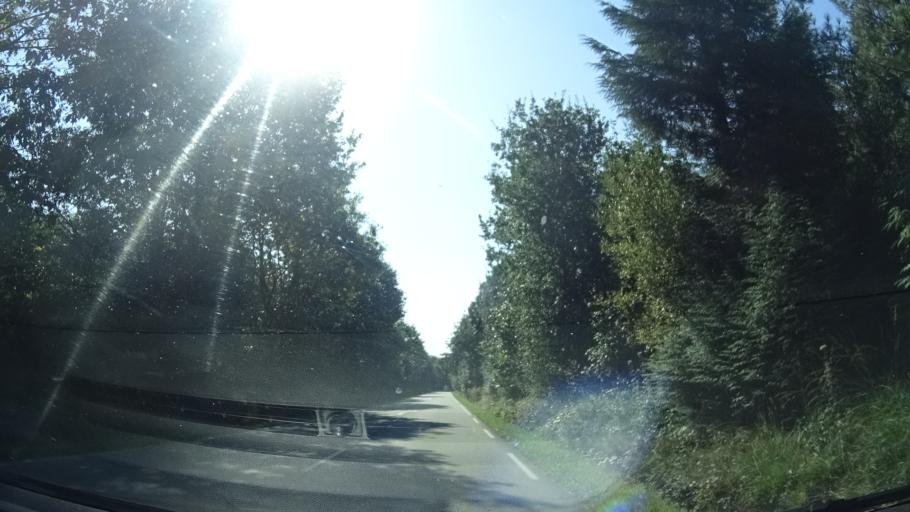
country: FR
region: Brittany
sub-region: Departement du Finistere
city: Cast
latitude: 48.1734
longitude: -4.1238
